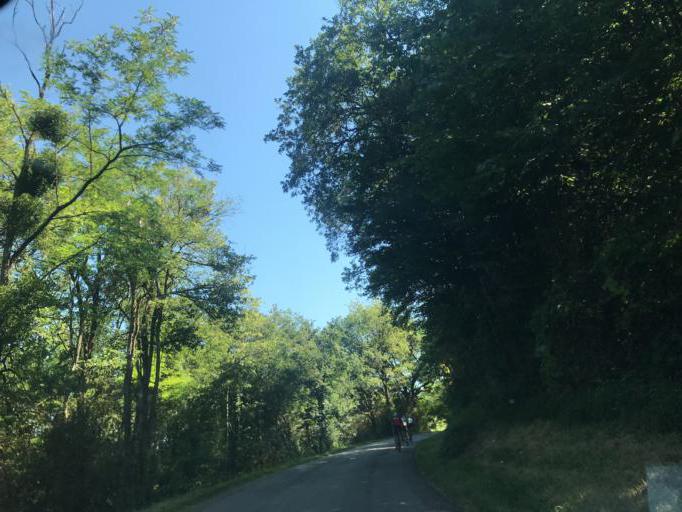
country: FR
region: Rhone-Alpes
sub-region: Departement de l'Ain
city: Saint-Martin-du-Mont
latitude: 46.0995
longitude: 5.3214
